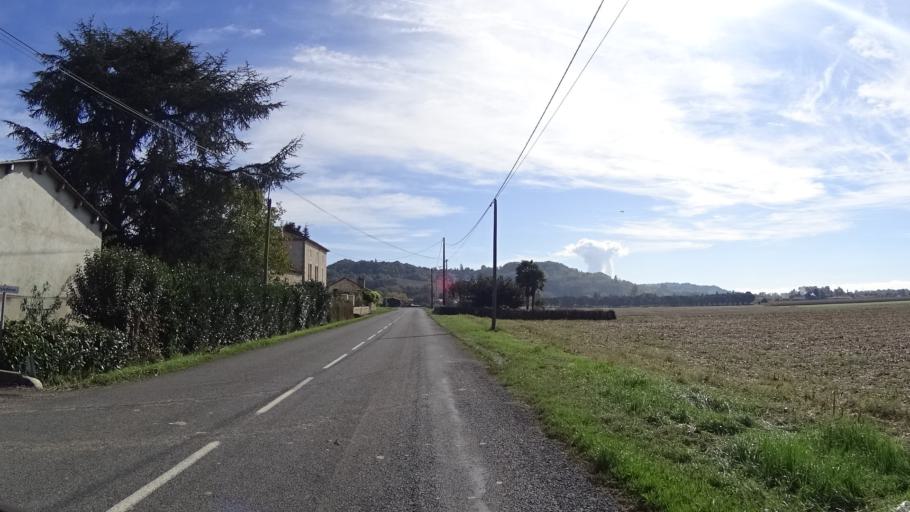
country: FR
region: Aquitaine
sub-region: Departement du Lot-et-Garonne
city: Castelculier
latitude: 44.1855
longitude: 0.6917
